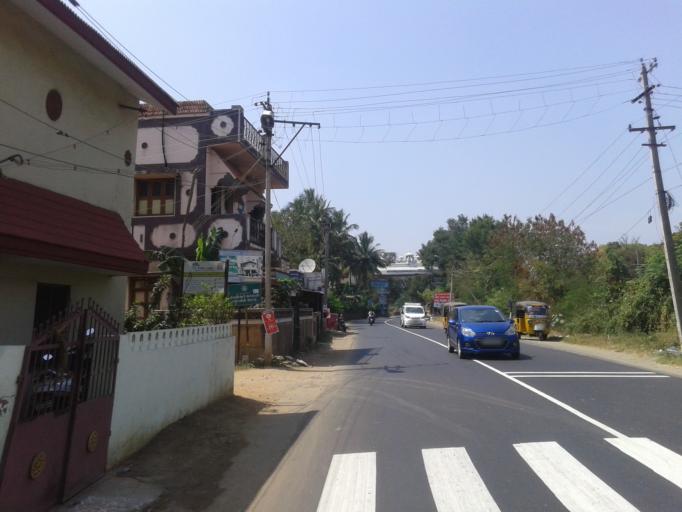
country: IN
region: Tamil Nadu
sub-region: Madurai
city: Madurai
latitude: 9.9368
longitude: 78.0741
